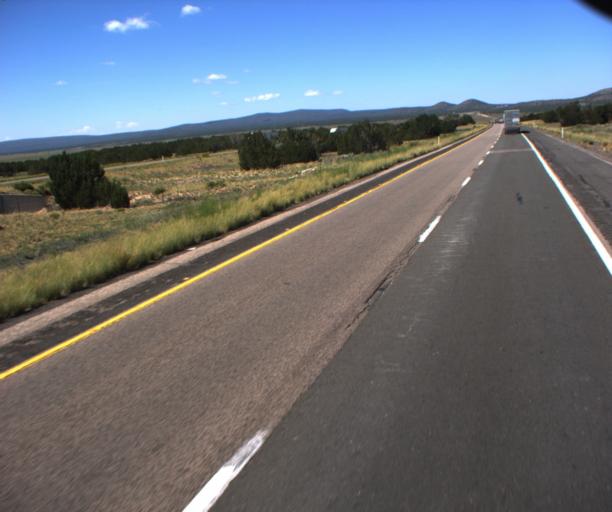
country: US
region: Arizona
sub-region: Mohave County
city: Peach Springs
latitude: 35.3187
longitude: -112.9548
